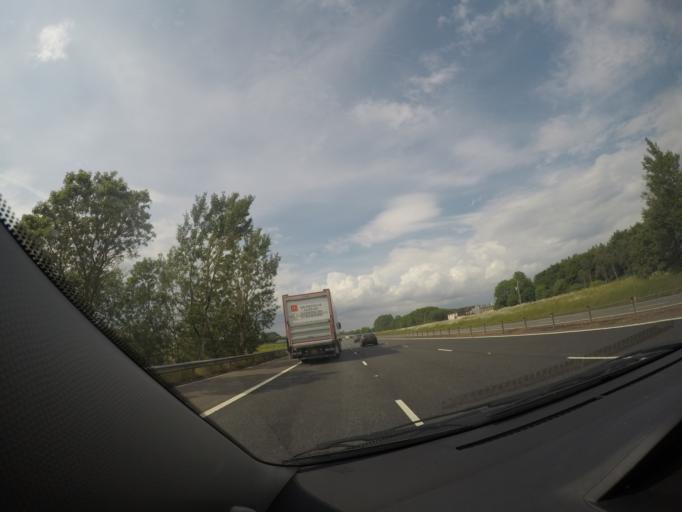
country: GB
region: Scotland
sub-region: Dumfries and Galloway
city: Lockerbie
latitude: 55.1555
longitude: -3.3846
